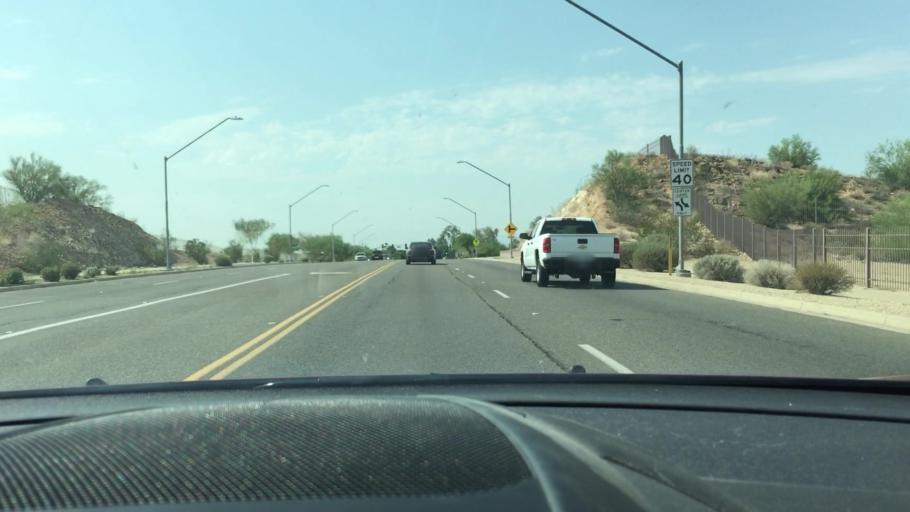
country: US
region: Arizona
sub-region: Maricopa County
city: Peoria
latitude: 33.6921
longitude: -112.2032
